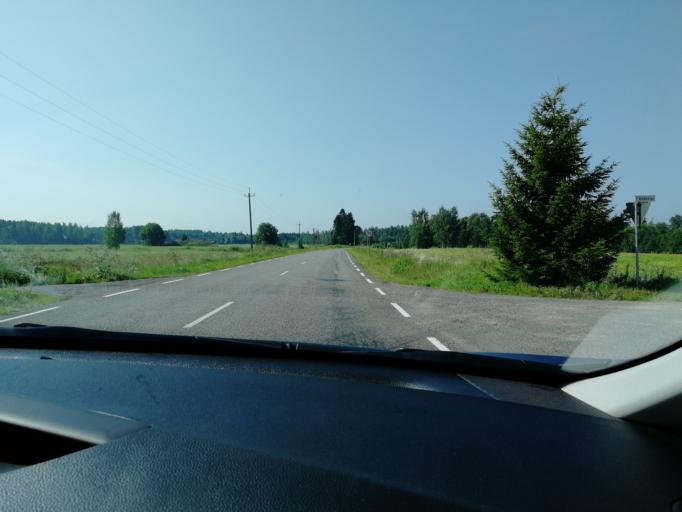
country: EE
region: Paernumaa
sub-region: Saarde vald
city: Kilingi-Nomme
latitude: 58.0239
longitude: 25.0094
